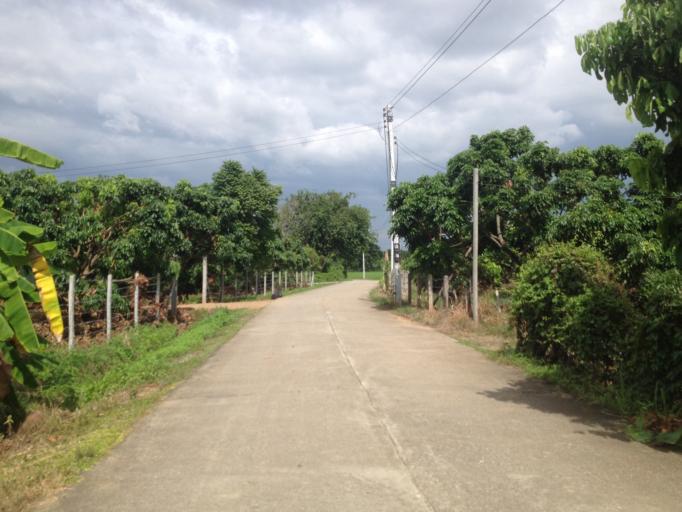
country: TH
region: Chiang Mai
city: Hang Dong
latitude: 18.6884
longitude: 98.9053
